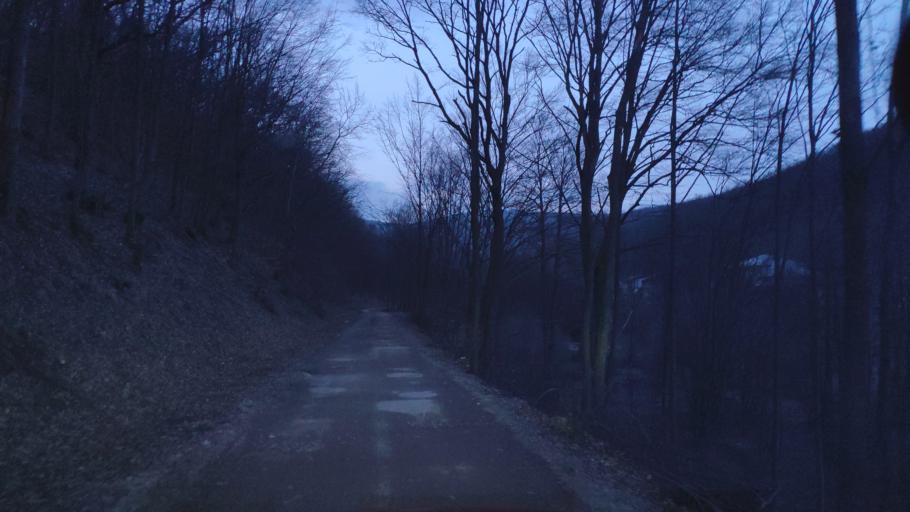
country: SK
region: Kosicky
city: Medzev
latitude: 48.7199
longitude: 20.9252
